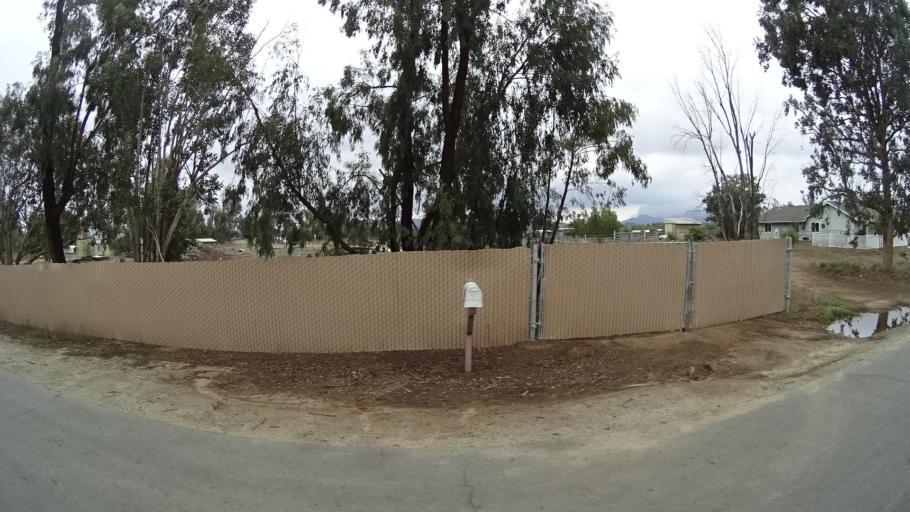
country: US
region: California
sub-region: San Diego County
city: Ramona
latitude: 33.0462
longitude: -116.9023
